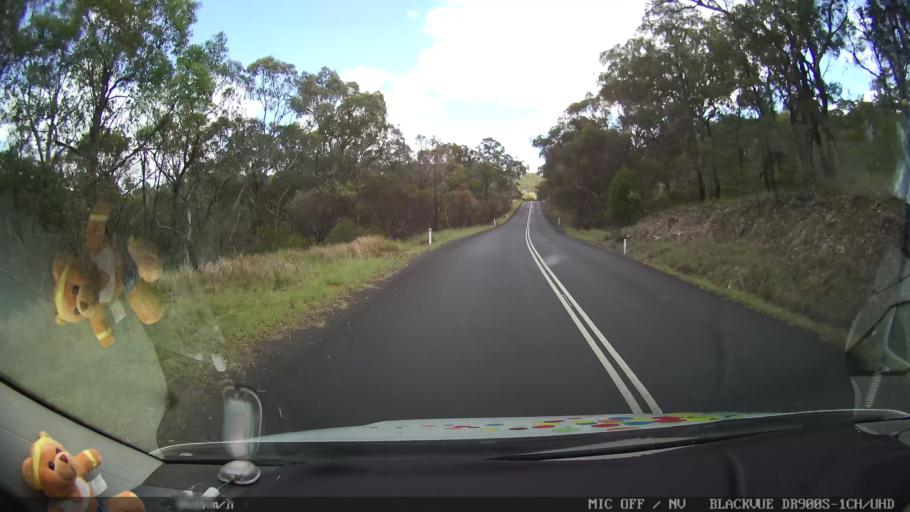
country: AU
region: New South Wales
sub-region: Glen Innes Severn
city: Glen Innes
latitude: -29.5436
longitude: 151.6684
